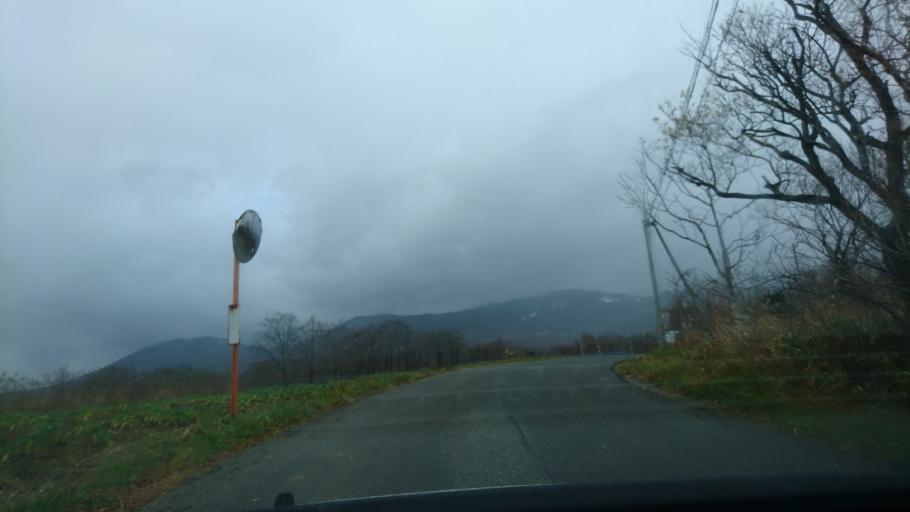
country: JP
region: Iwate
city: Ichinoseki
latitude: 38.9268
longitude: 140.8407
